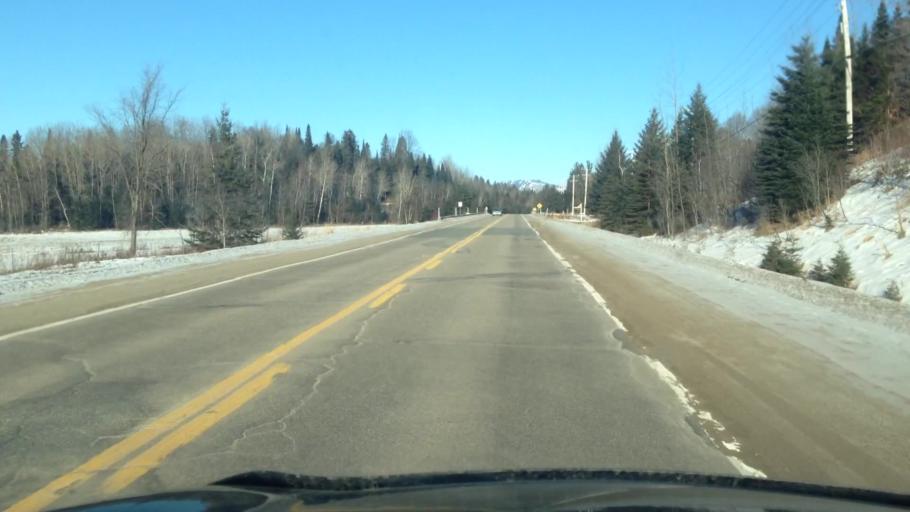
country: CA
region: Quebec
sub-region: Laurentides
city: Mont-Tremblant
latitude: 46.0824
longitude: -74.6126
